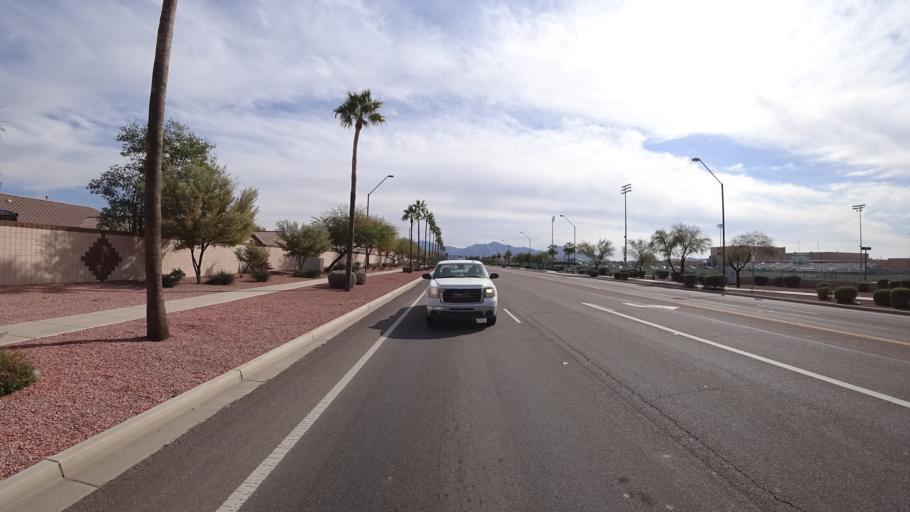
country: US
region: Arizona
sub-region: Maricopa County
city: Avondale
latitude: 33.4275
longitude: -112.3063
